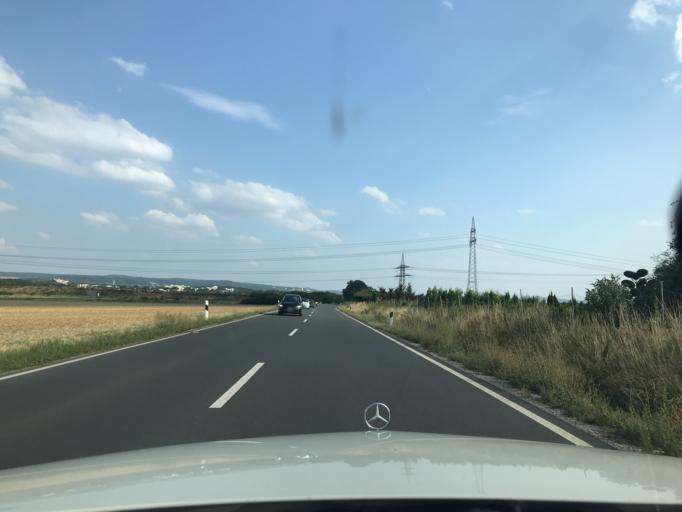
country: DE
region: Lower Saxony
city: Bovenden
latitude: 51.5713
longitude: 9.8798
